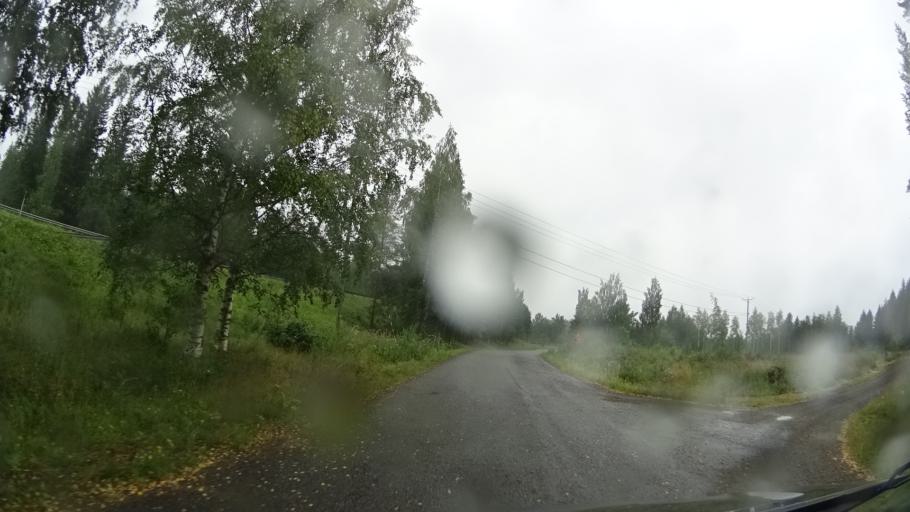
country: FI
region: North Karelia
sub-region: Keski-Karjala
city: Raeaekkylae
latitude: 62.3171
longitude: 29.5116
